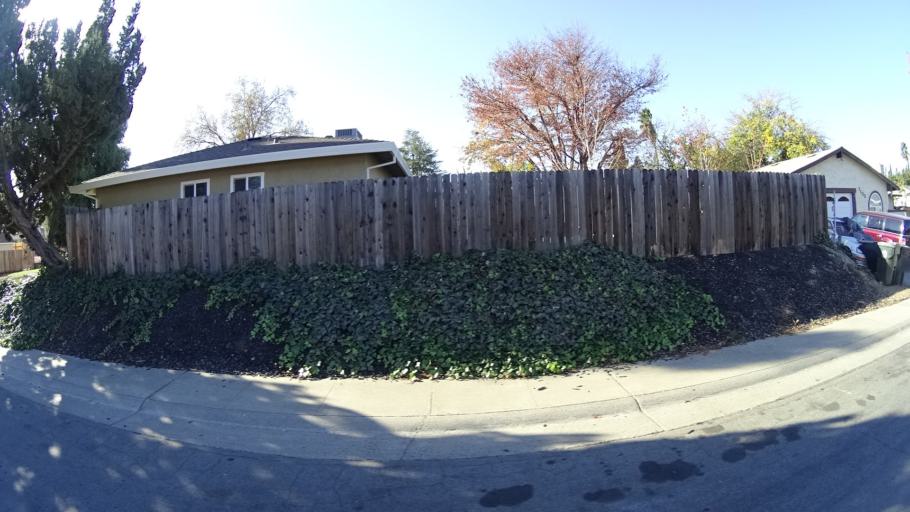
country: US
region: California
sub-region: Sacramento County
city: Fair Oaks
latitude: 38.6721
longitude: -121.2976
